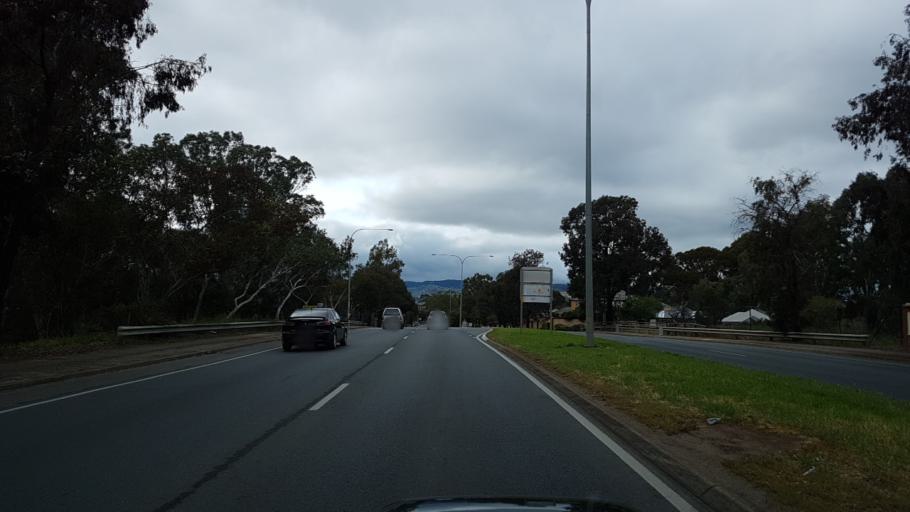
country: AU
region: South Australia
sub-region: Norwood Payneham St Peters
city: Marden
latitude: -34.8903
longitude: 138.6308
